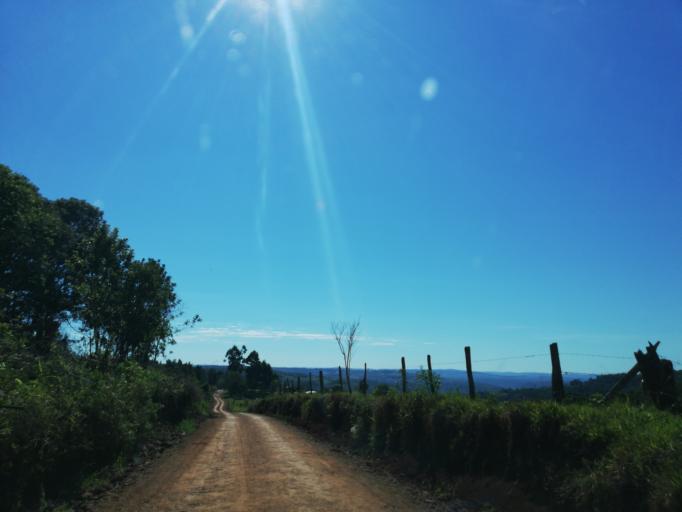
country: AR
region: Misiones
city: Dos de Mayo
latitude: -27.0771
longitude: -54.4020
